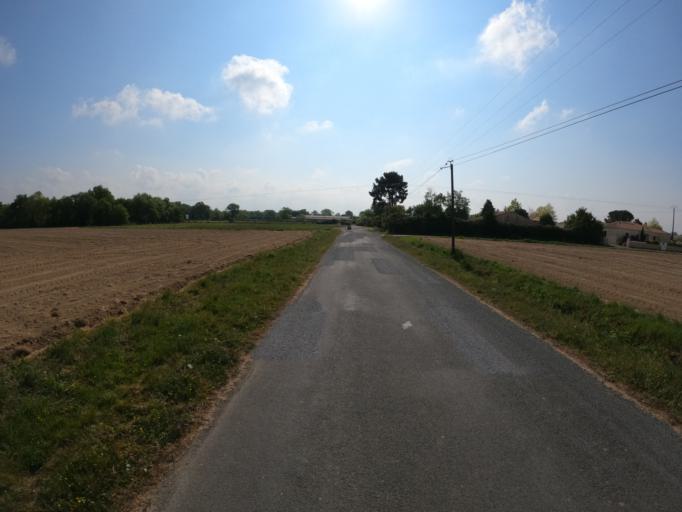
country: FR
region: Pays de la Loire
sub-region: Departement de la Vendee
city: Montaigu
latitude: 47.0049
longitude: -1.2873
